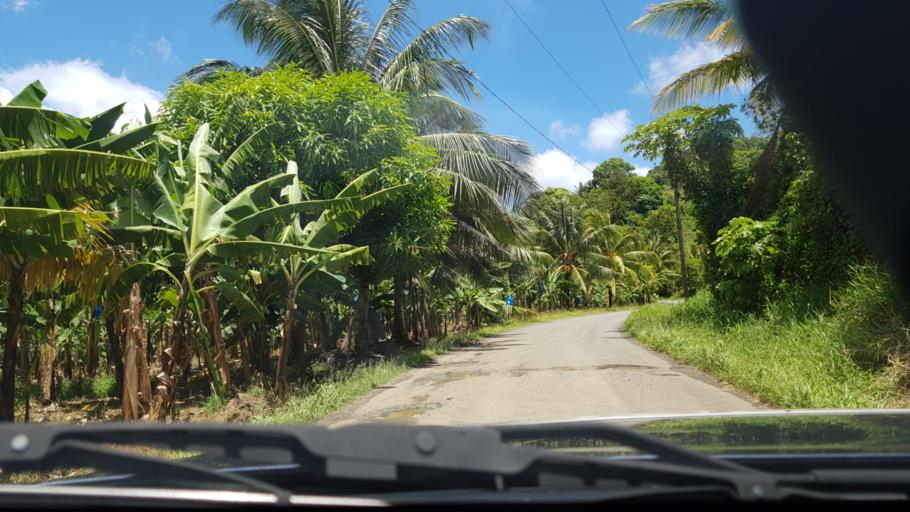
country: LC
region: Anse-la-Raye
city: Anse La Raye
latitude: 13.9479
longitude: -60.9914
